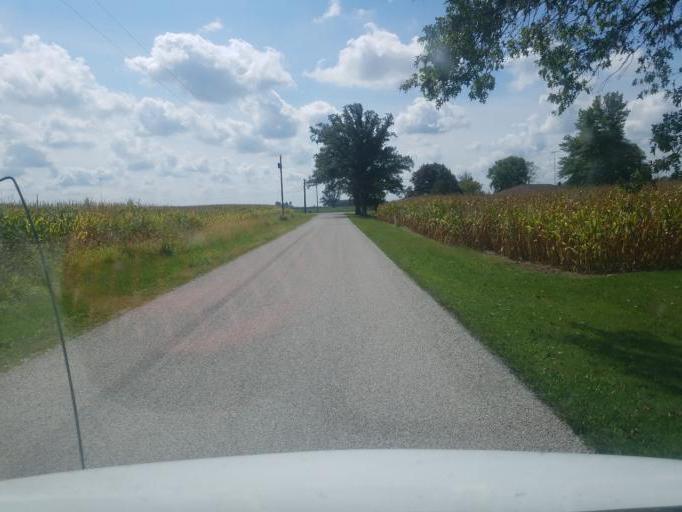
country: US
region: Ohio
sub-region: Marion County
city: Prospect
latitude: 40.4531
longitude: -83.1353
